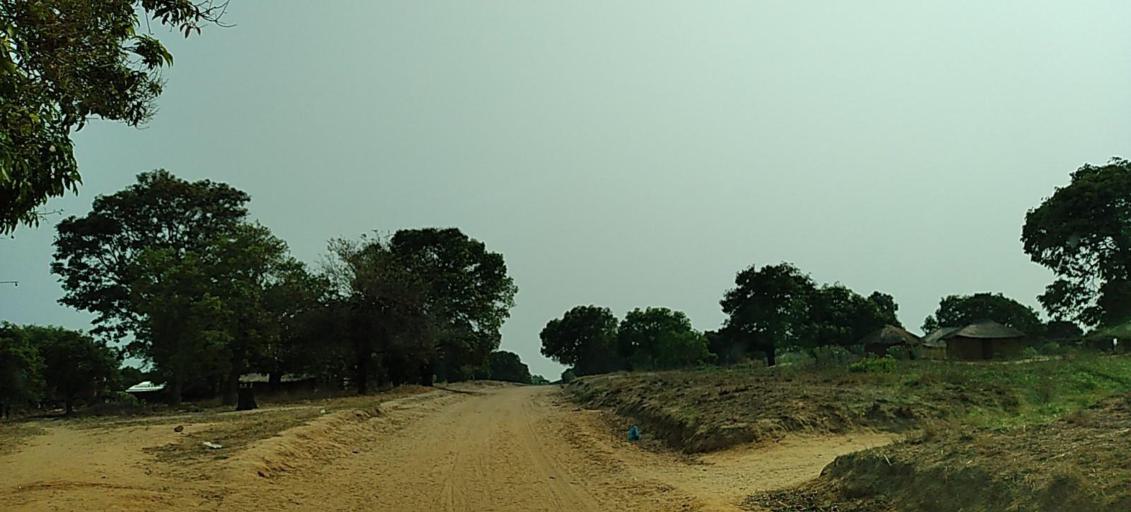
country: ZM
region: North-Western
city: Zambezi
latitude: -13.1729
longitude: 23.4030
